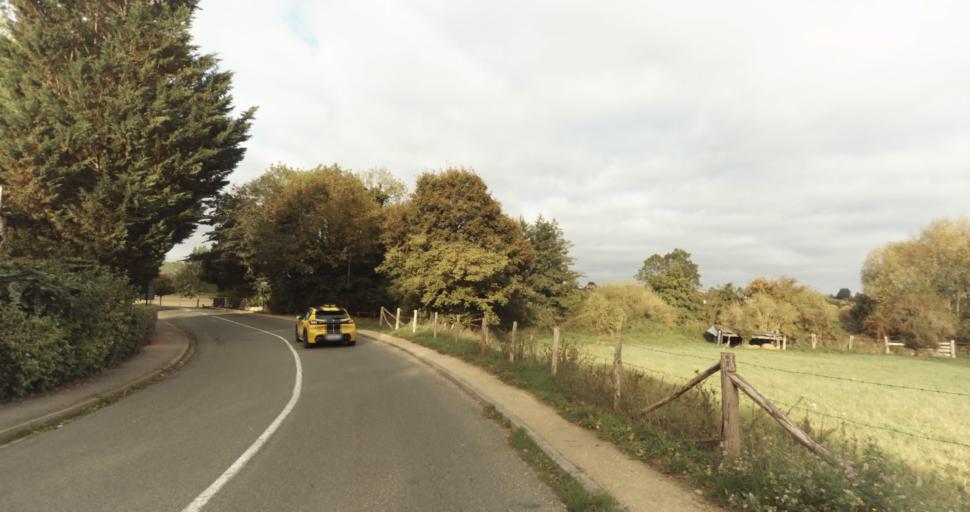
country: FR
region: Centre
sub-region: Departement d'Eure-et-Loir
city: Vernouillet
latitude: 48.7209
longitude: 1.3548
